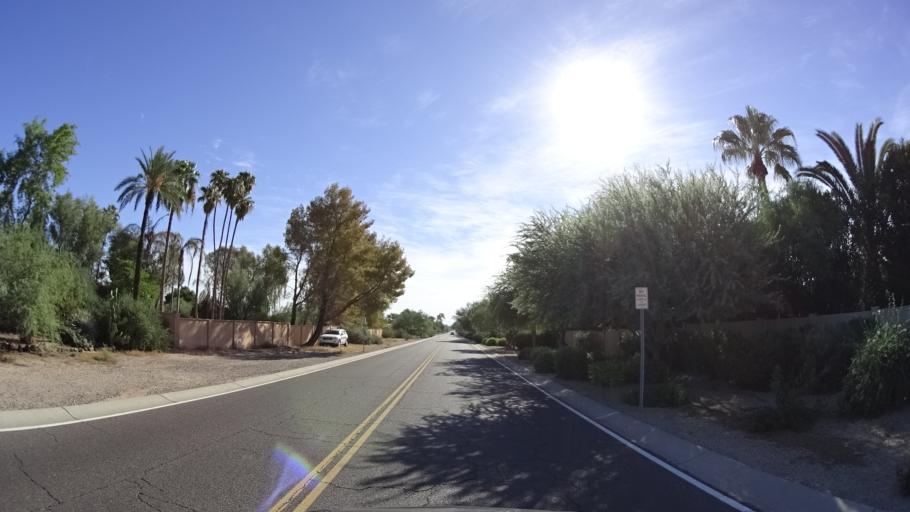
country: US
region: Arizona
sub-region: Maricopa County
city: Paradise Valley
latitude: 33.5166
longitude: -111.9390
